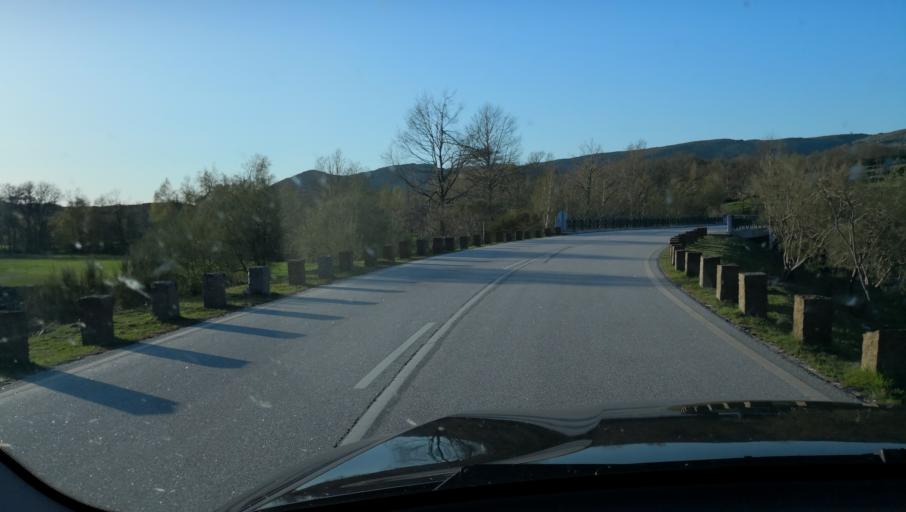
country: PT
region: Vila Real
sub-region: Vila Real
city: Vila Real
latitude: 41.3679
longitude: -7.8012
